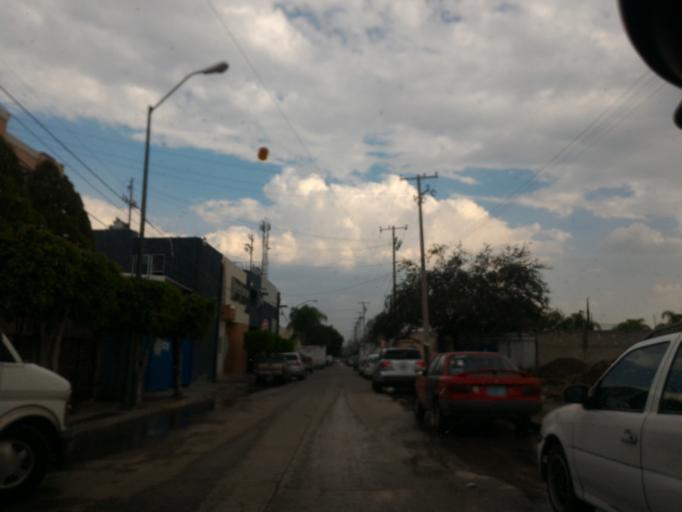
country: MX
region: Guanajuato
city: San Francisco del Rincon
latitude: 21.0363
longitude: -101.8584
